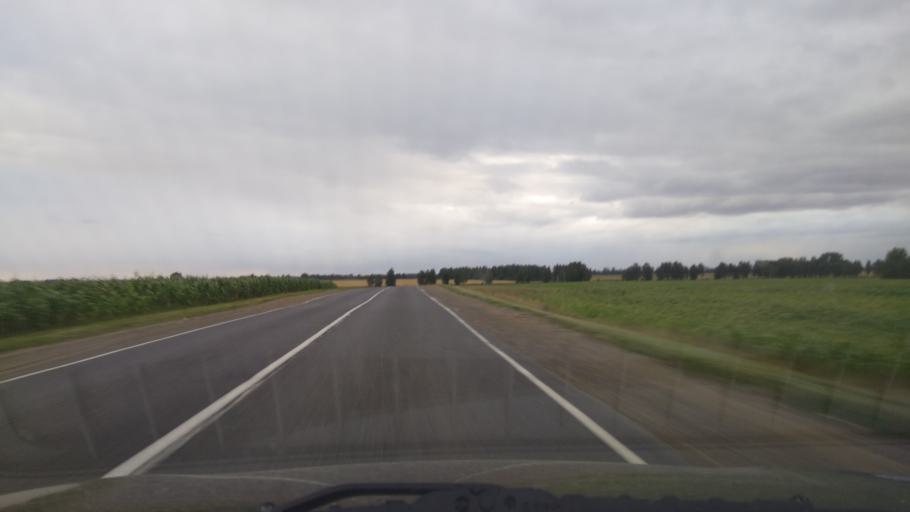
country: BY
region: Brest
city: Byaroza
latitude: 52.4337
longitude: 24.9803
